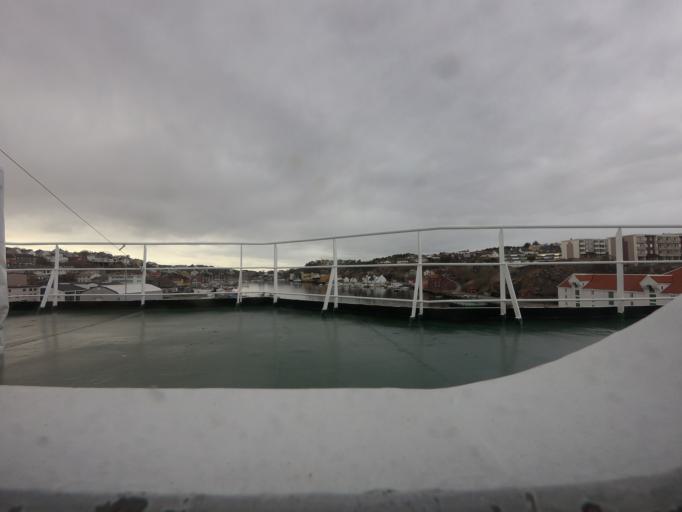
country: NO
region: More og Romsdal
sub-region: Kristiansund
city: Kristiansund
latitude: 63.1146
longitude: 7.7376
